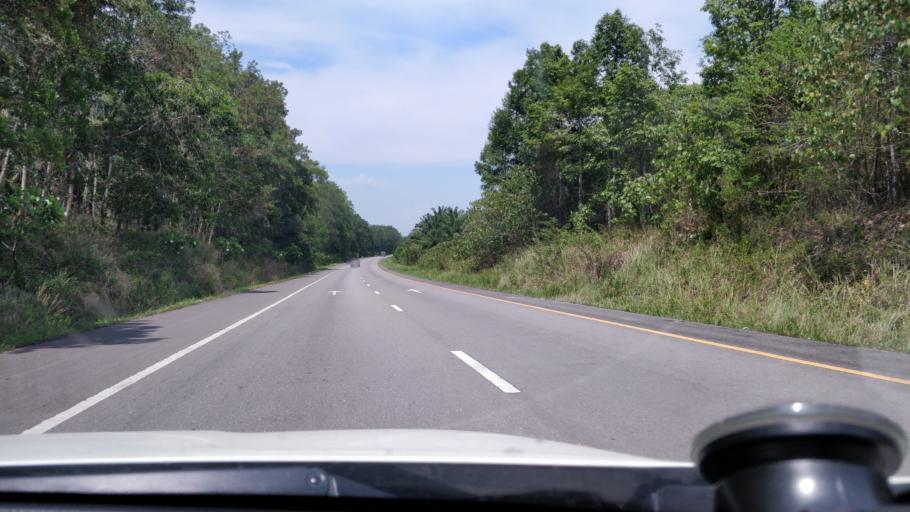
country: TH
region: Surat Thani
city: Chai Buri
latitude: 8.6381
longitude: 99.0206
